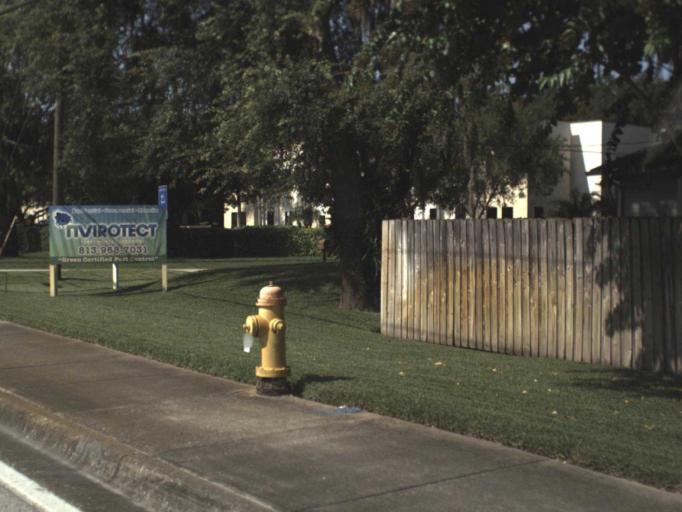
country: US
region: Florida
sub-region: Hillsborough County
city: Lake Magdalene
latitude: 28.1016
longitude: -82.4606
